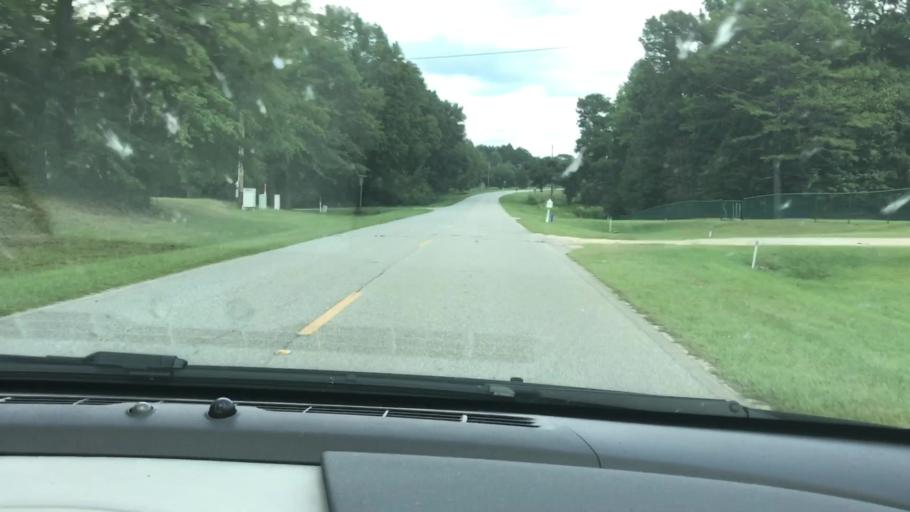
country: US
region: Georgia
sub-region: Clay County
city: Fort Gaines
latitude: 31.7187
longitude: -85.0581
